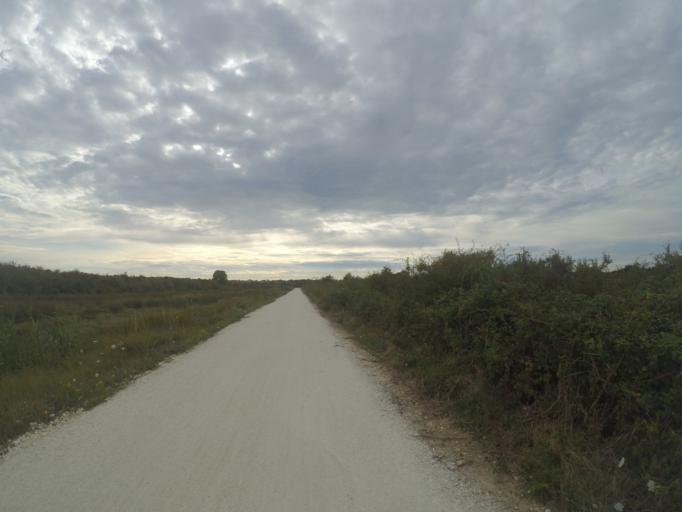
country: FR
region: Poitou-Charentes
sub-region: Departement de la Charente-Maritime
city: Meschers-sur-Gironde
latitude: 45.5577
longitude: -0.9362
